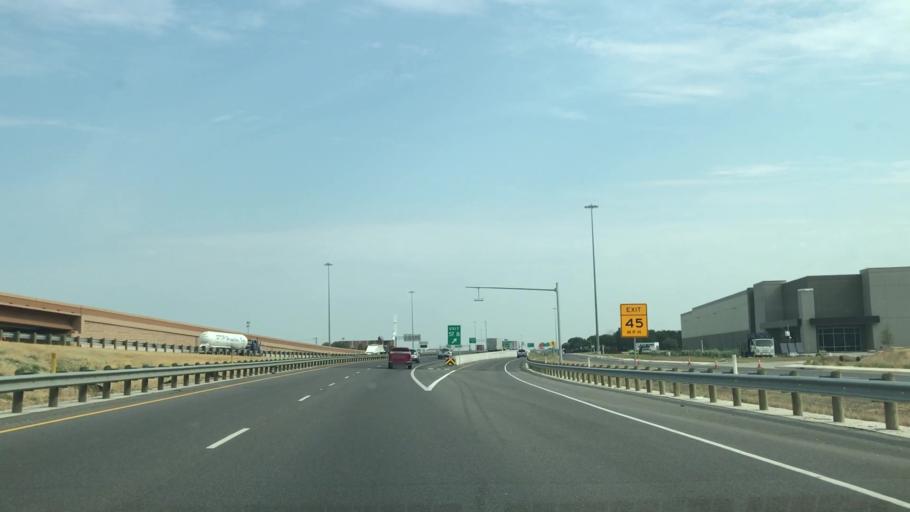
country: US
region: Texas
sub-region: Tarrant County
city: Blue Mound
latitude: 32.8432
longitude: -97.3119
